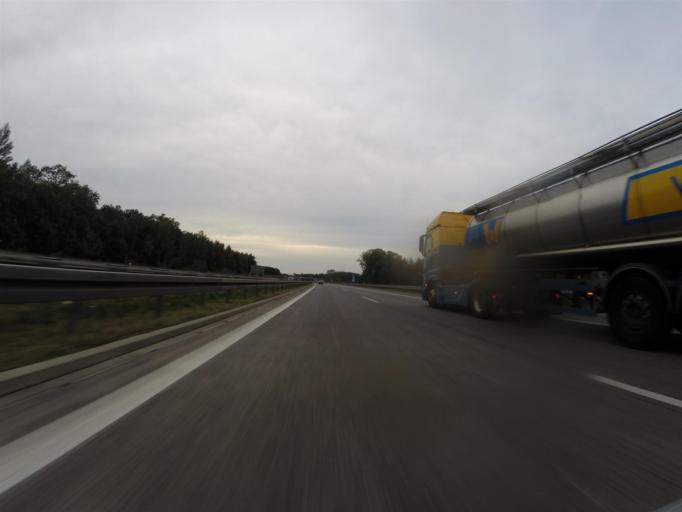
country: DE
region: Saxony
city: Naunhof
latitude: 51.3022
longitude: 12.6072
